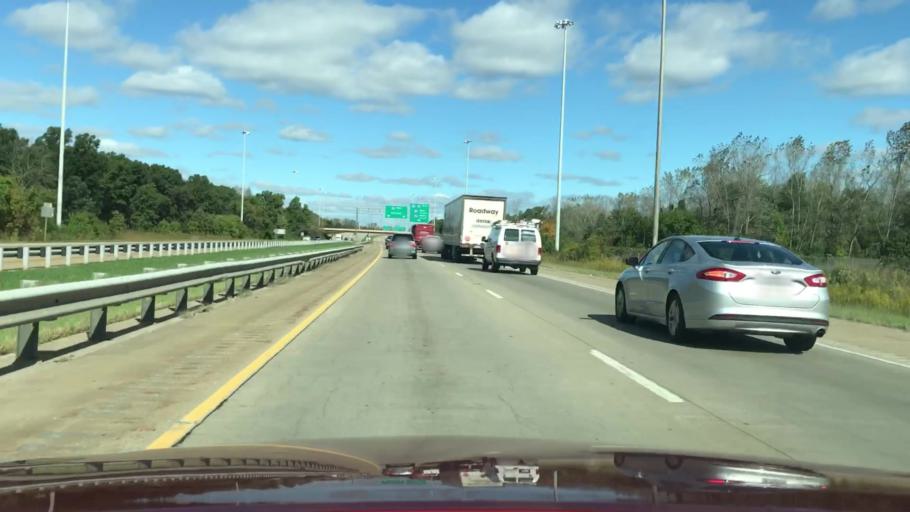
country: US
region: Illinois
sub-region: Cook County
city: Thornton
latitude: 41.5656
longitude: -87.5834
